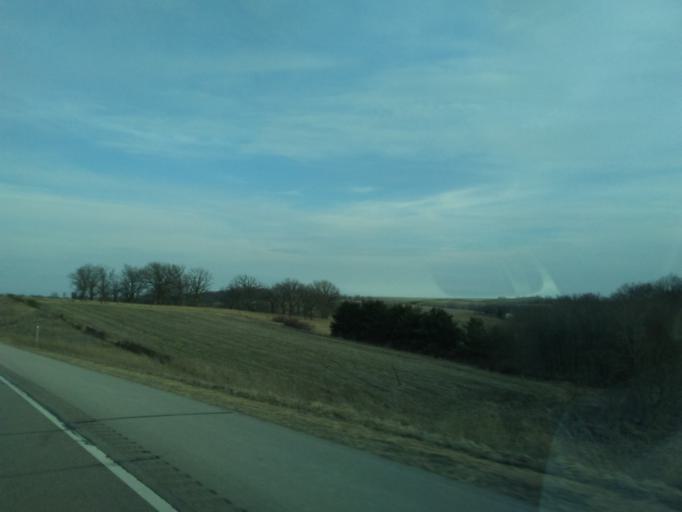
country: US
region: Wisconsin
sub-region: Iowa County
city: Dodgeville
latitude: 42.9663
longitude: -90.0760
